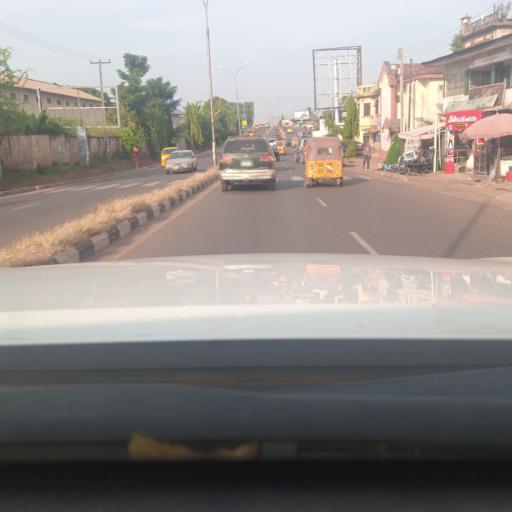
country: NG
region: Enugu
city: Enugu
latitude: 6.4487
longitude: 7.5007
